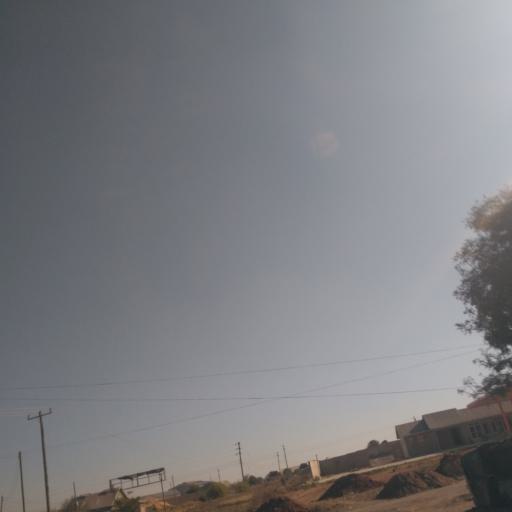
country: TZ
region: Dodoma
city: Dodoma
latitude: -6.1582
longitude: 35.7120
